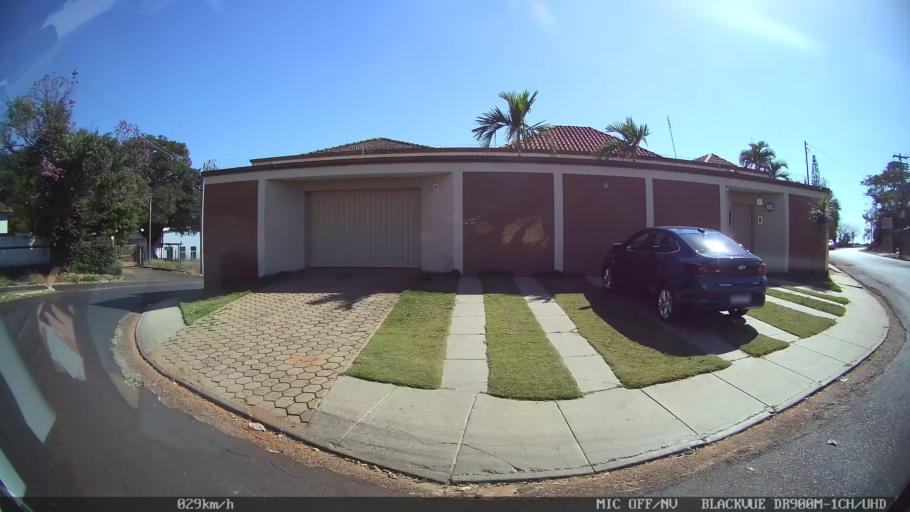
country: BR
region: Sao Paulo
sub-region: Batatais
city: Batatais
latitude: -20.8818
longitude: -47.6023
